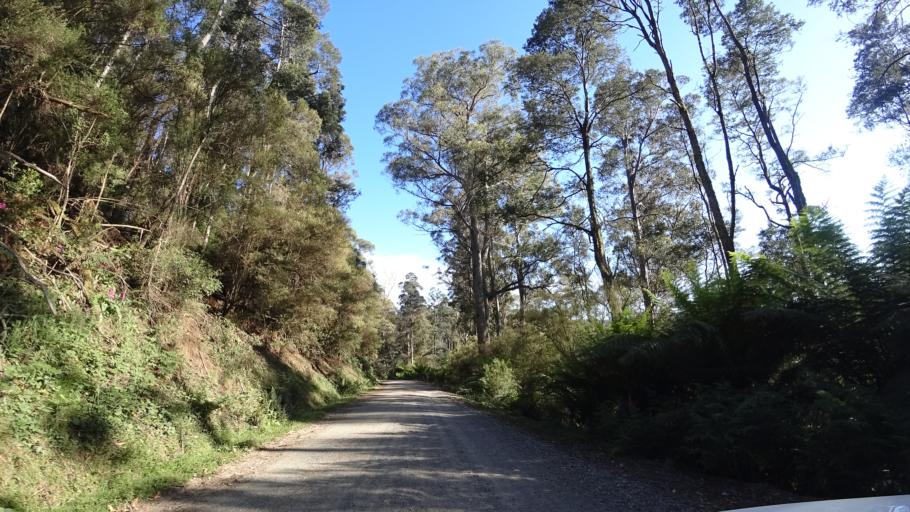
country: AU
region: Tasmania
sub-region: Break O'Day
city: St Helens
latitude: -41.2645
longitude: 148.0257
